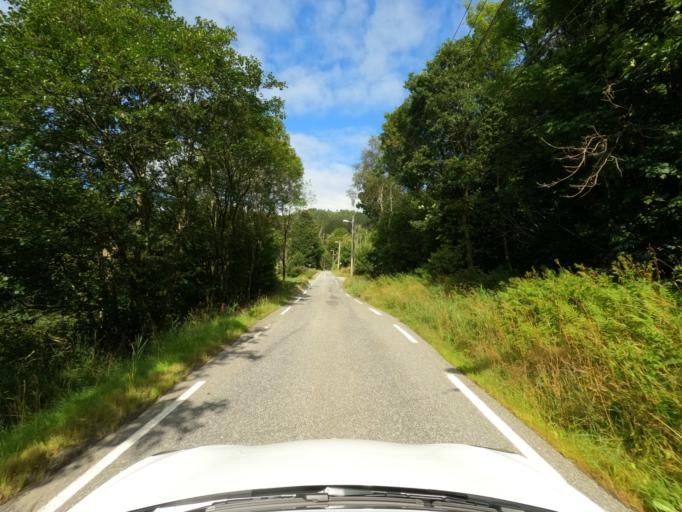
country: NO
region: Hordaland
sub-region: Bergen
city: Sandsli
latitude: 60.2746
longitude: 5.3532
